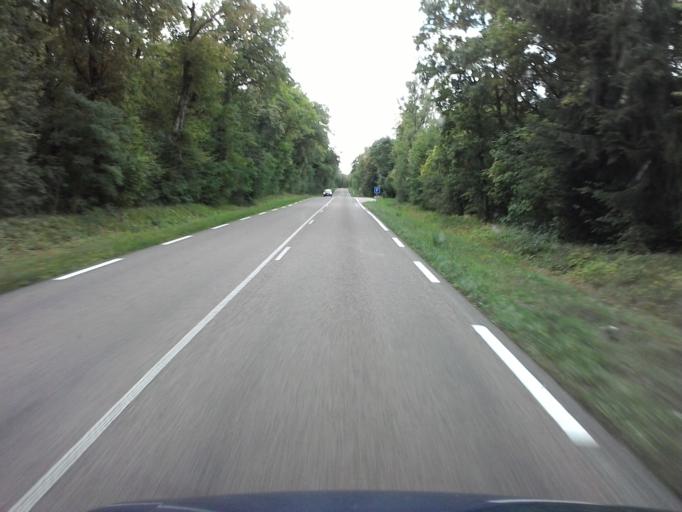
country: FR
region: Lorraine
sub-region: Departement des Vosges
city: Neufchateau
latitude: 48.3417
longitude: 5.6555
